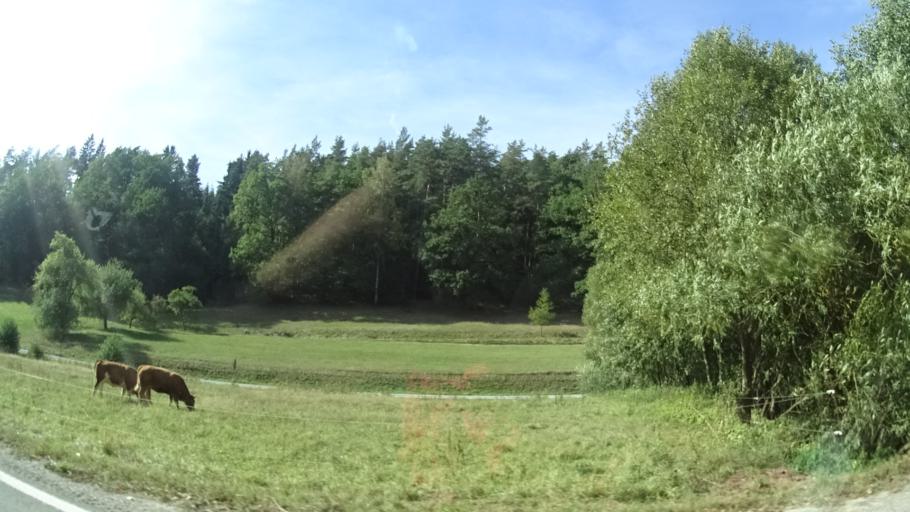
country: DE
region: Thuringia
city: Wallbach
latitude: 50.6333
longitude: 10.3972
